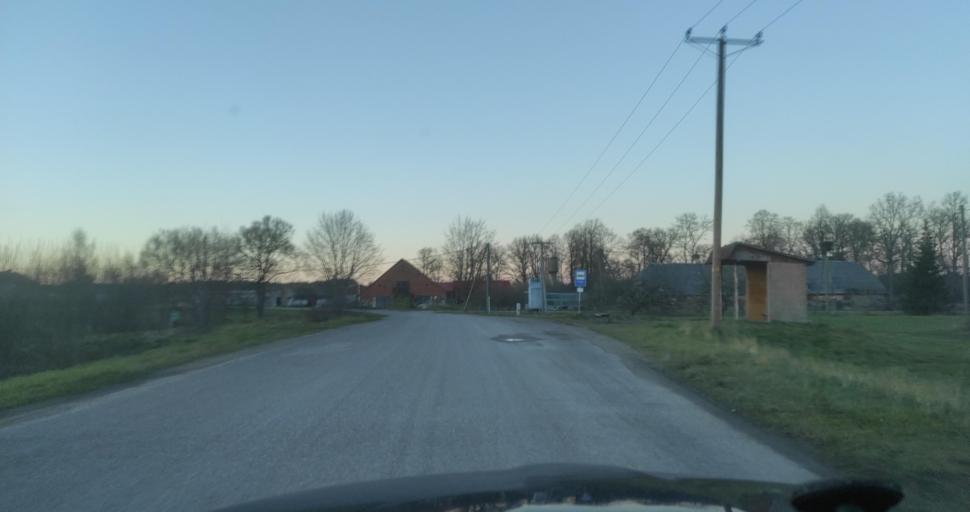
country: LV
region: Dundaga
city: Dundaga
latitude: 57.3746
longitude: 22.2307
